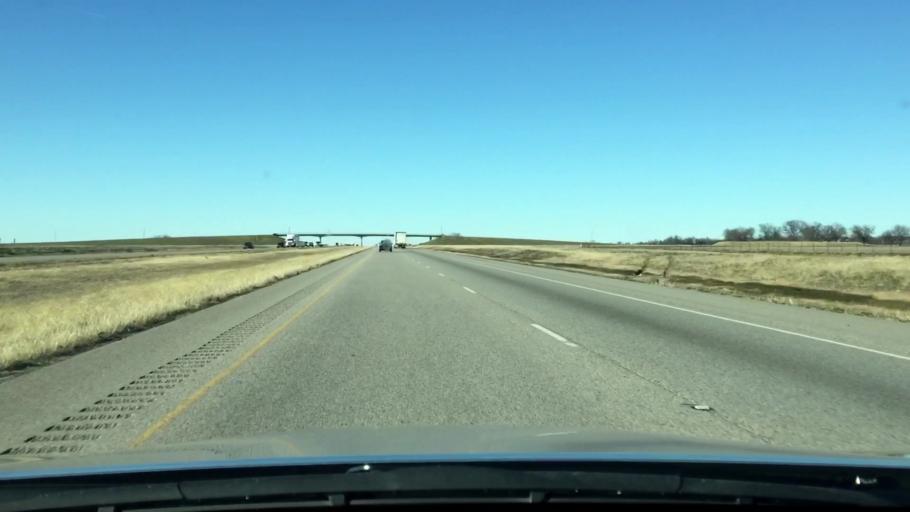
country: US
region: Texas
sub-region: Hill County
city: Itasca
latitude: 32.1217
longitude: -97.1166
